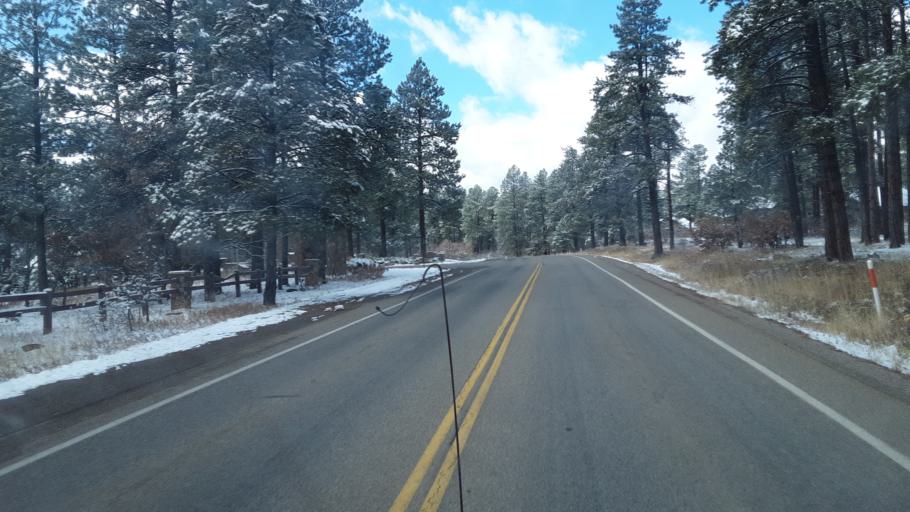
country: US
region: Colorado
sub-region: La Plata County
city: Durango
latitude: 37.3121
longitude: -107.7874
